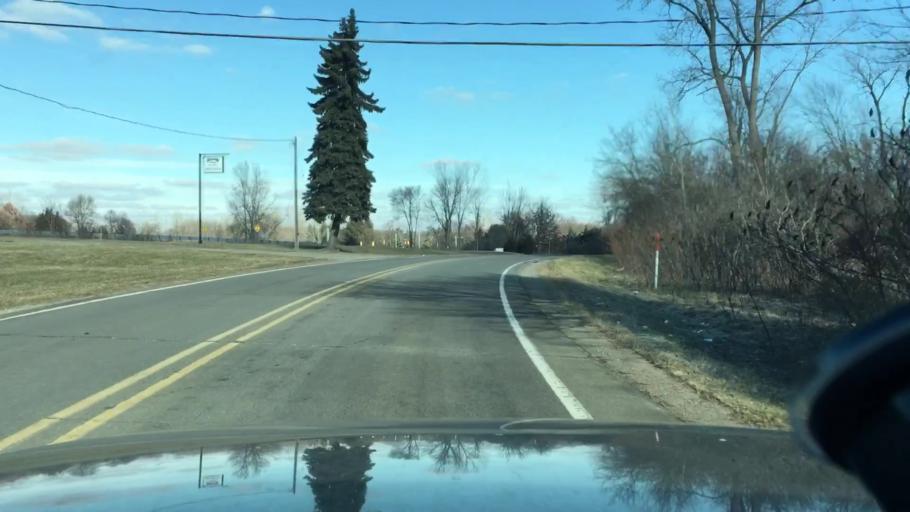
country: US
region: Michigan
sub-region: Jackson County
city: Jackson
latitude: 42.2883
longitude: -84.4312
